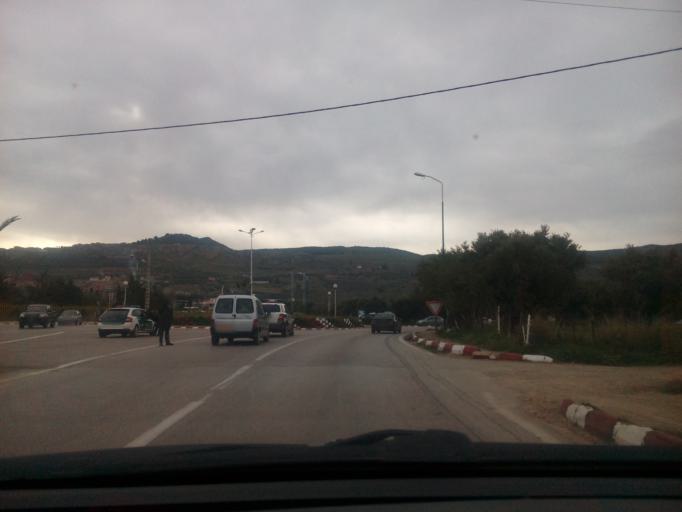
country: DZ
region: Tlemcen
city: Mansoura
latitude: 34.8676
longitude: -1.3494
